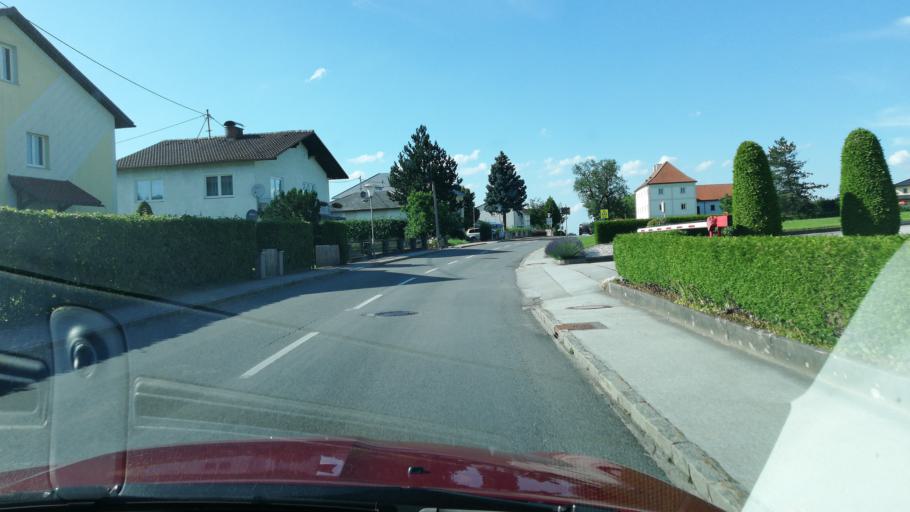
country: AT
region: Upper Austria
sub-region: Politischer Bezirk Steyr-Land
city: Pfarrkirchen bei Bad Hall
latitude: 47.9933
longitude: 14.2173
